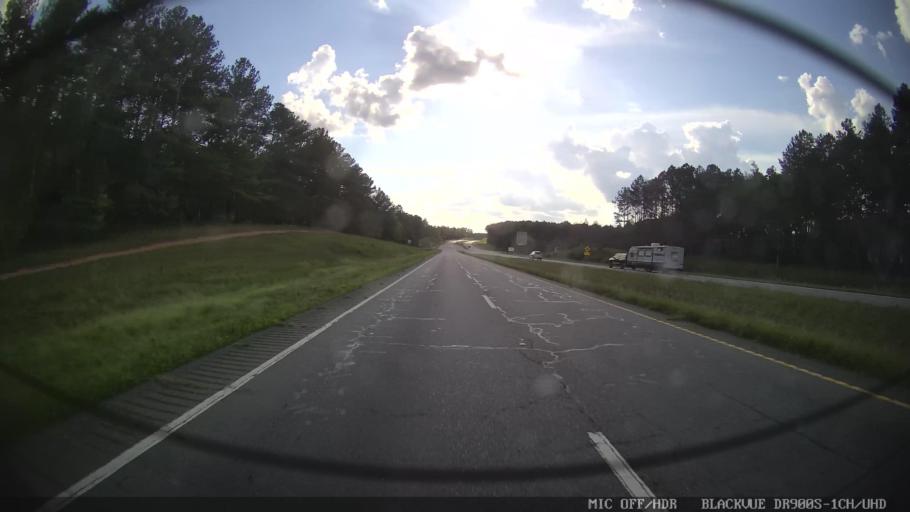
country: US
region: Georgia
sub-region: Bartow County
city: Euharlee
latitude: 34.2036
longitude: -85.0258
